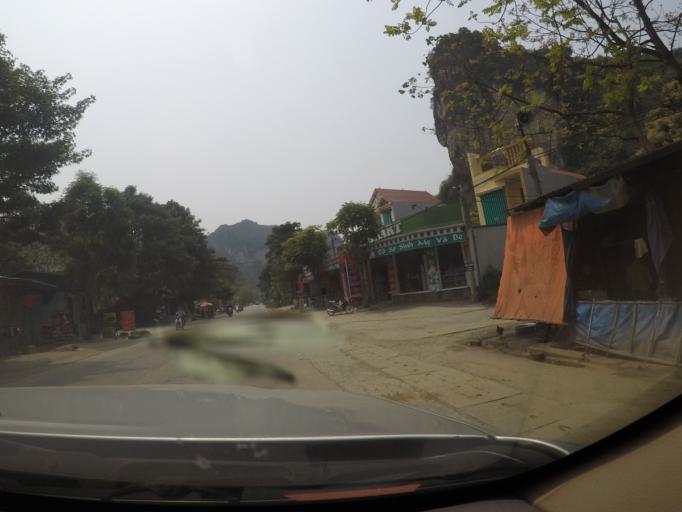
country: VN
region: Thanh Hoa
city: Thi Tran Cam Thuy
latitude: 20.2237
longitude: 105.4919
